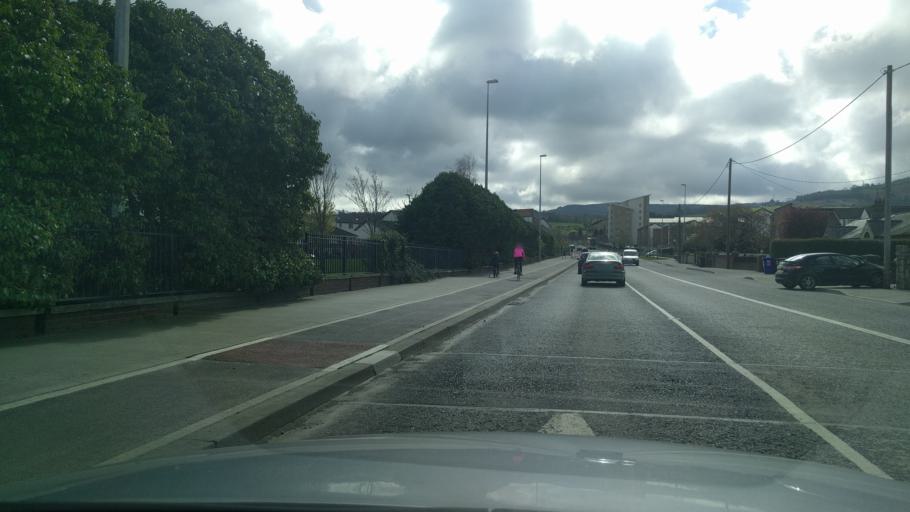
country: IE
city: Knocklyon
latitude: 53.2735
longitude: -6.3305
